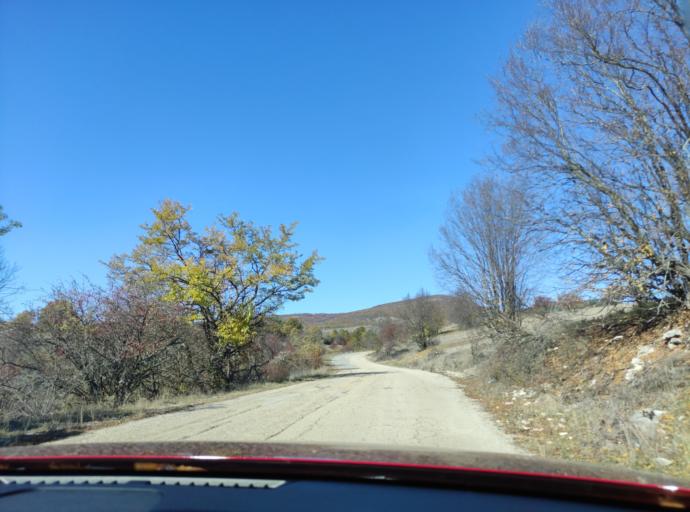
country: BG
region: Montana
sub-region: Obshtina Montana
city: Montana
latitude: 43.4428
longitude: 23.0497
